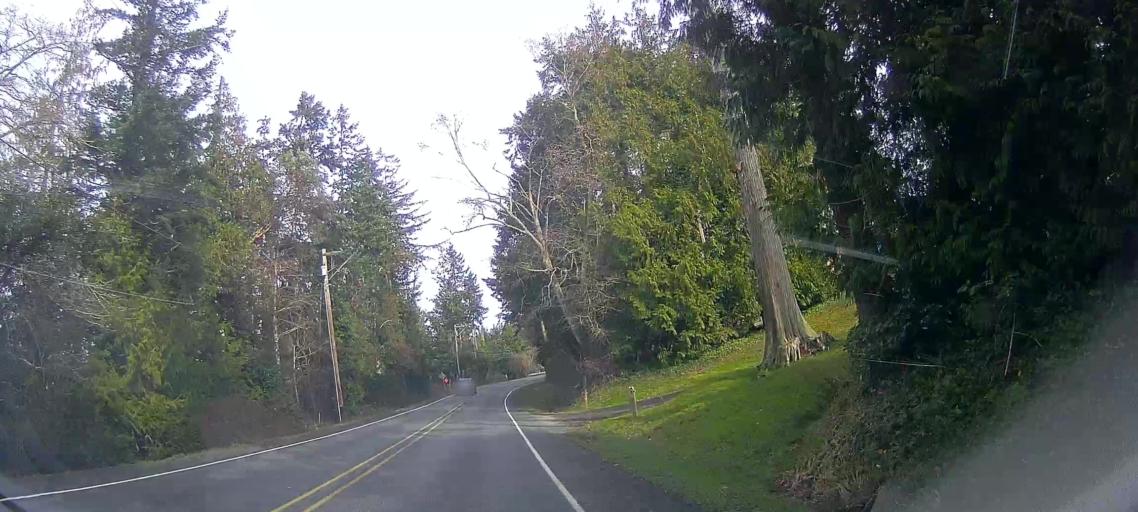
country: US
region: Washington
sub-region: Island County
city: Camano
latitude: 48.2527
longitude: -122.4749
